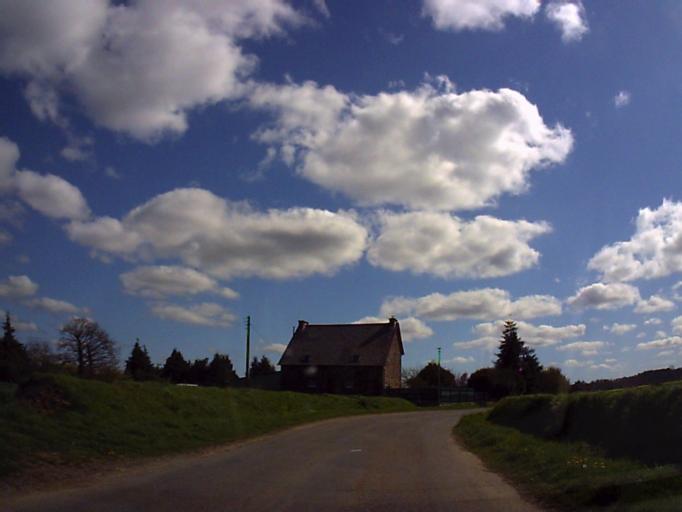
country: FR
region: Brittany
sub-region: Departement d'Ille-et-Vilaine
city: Boisgervilly
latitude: 48.0994
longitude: -2.1174
